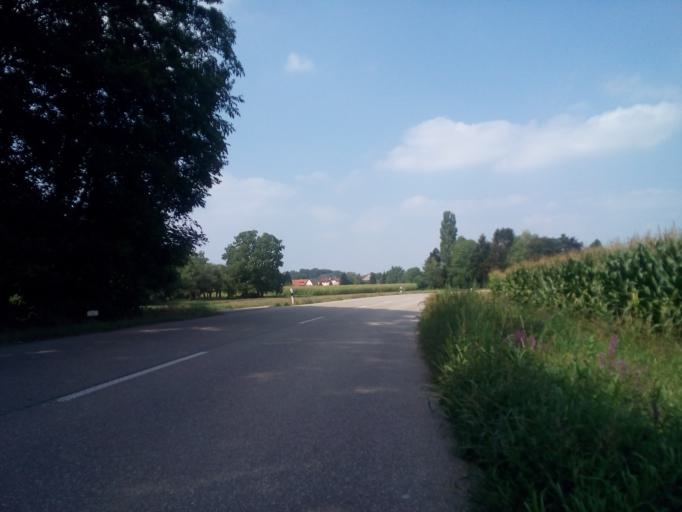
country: DE
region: Baden-Wuerttemberg
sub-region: Freiburg Region
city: Rheinau
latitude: 48.6452
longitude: 7.8974
